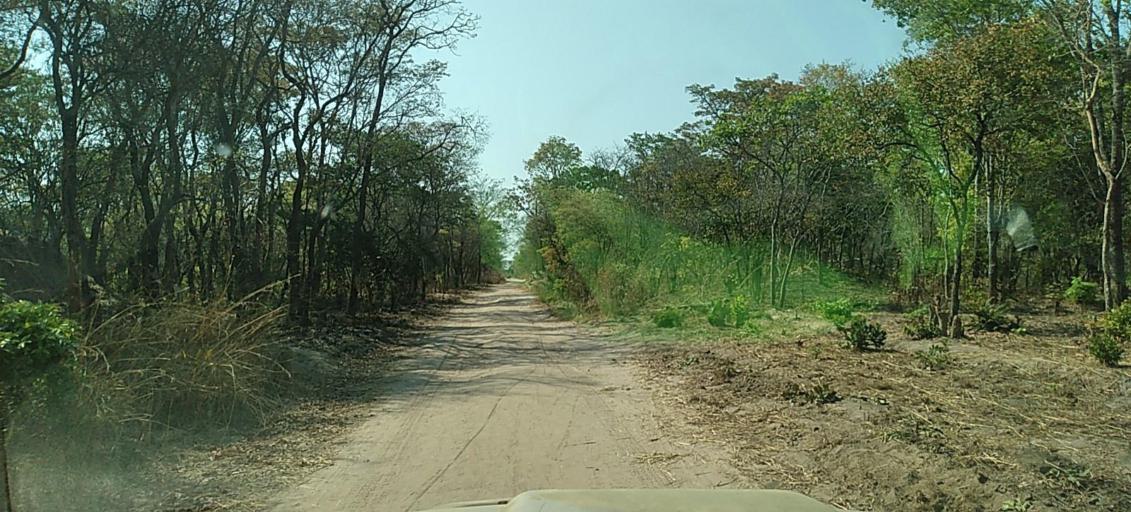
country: ZM
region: North-Western
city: Kalengwa
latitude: -13.3515
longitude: 24.8544
